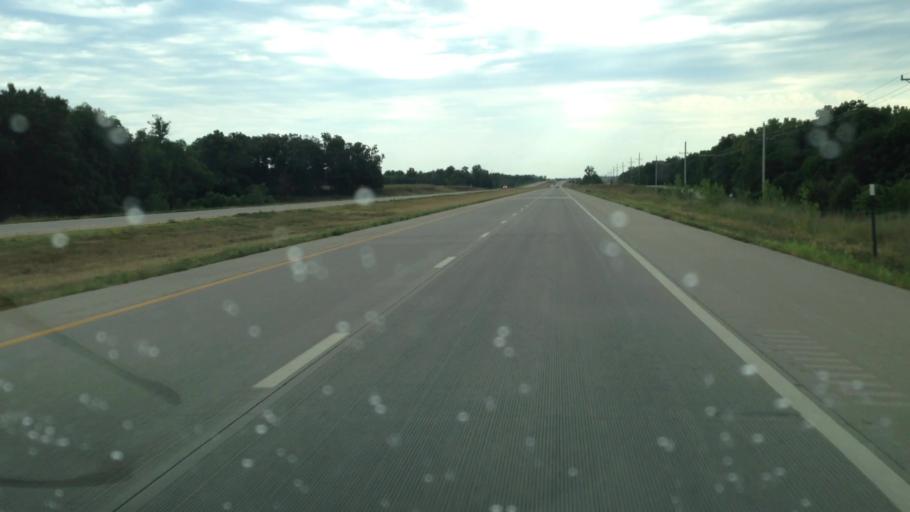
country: US
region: Kansas
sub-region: Douglas County
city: Baldwin City
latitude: 38.7524
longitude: -95.2680
